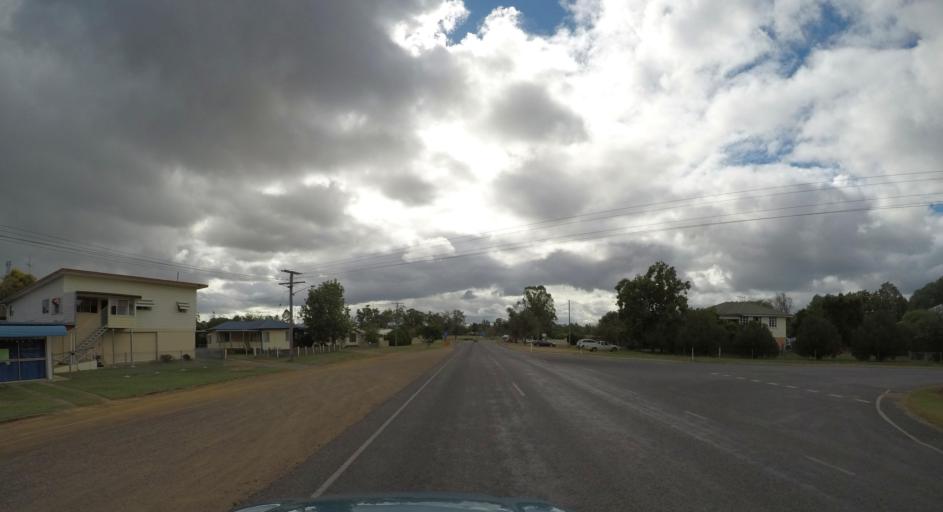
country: AU
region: Queensland
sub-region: North Burnett
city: Gayndah
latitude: -25.5883
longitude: 151.3013
